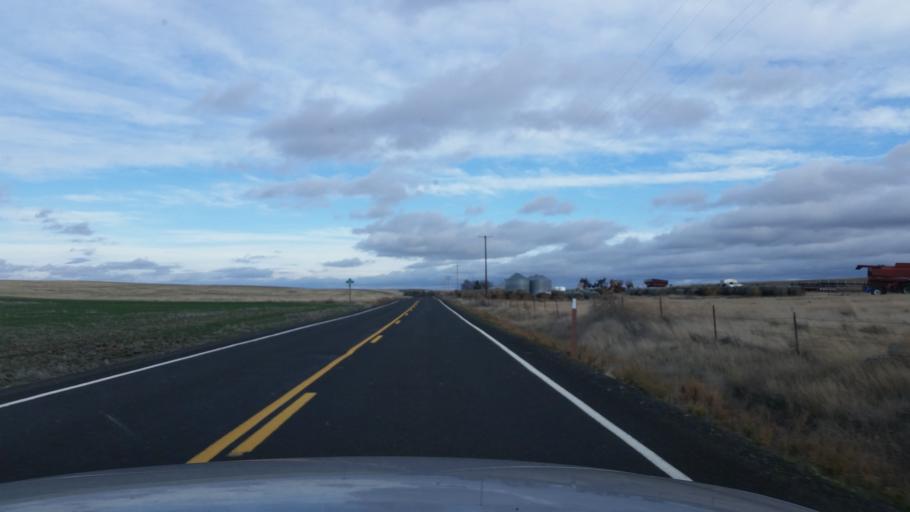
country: US
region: Washington
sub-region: Lincoln County
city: Davenport
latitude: 47.3510
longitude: -118.0706
